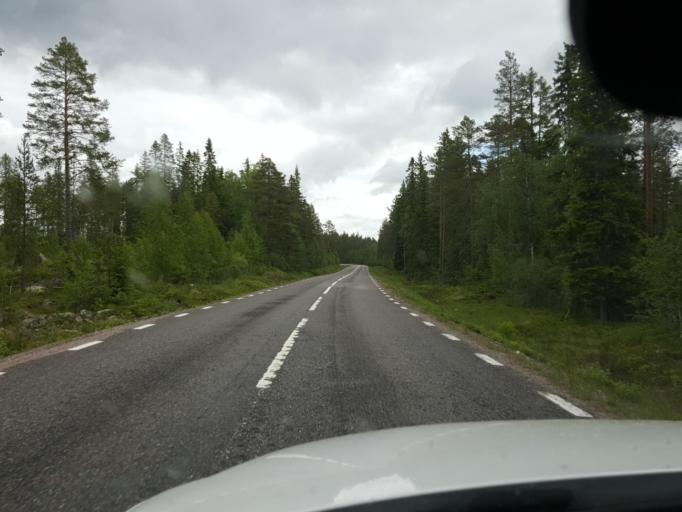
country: SE
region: Gaevleborg
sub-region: Ljusdals Kommun
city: Farila
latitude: 61.7549
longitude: 15.4408
